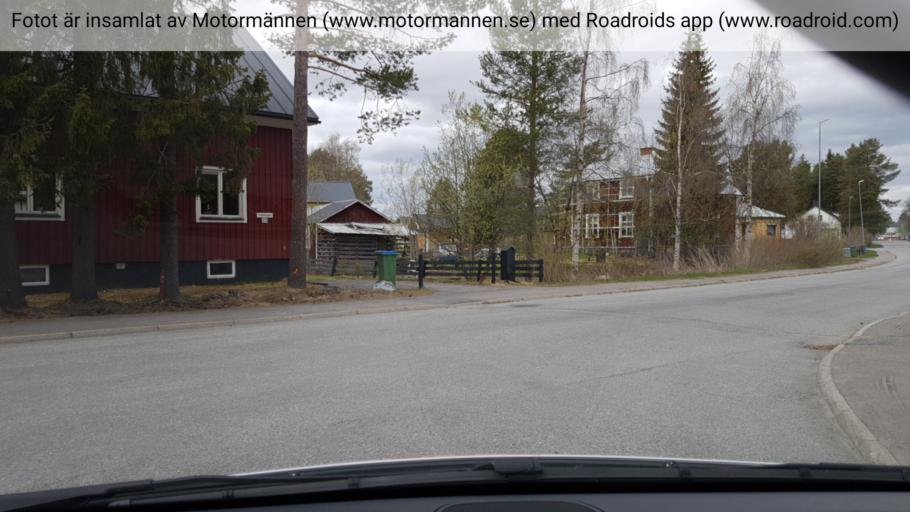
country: SE
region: Vaesterbotten
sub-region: Sorsele Kommun
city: Sorsele
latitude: 65.5313
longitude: 17.5385
